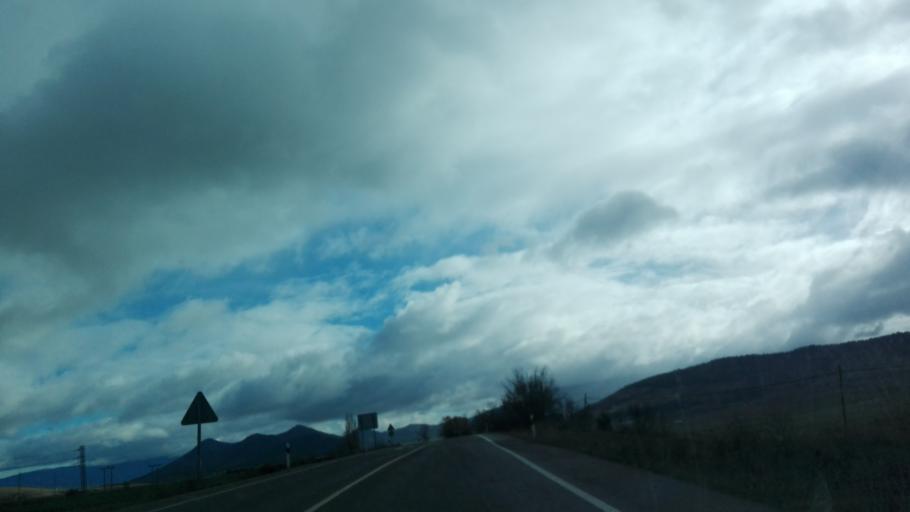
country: ES
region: Navarre
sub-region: Provincia de Navarra
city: Lizoain
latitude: 42.7946
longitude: -1.4785
